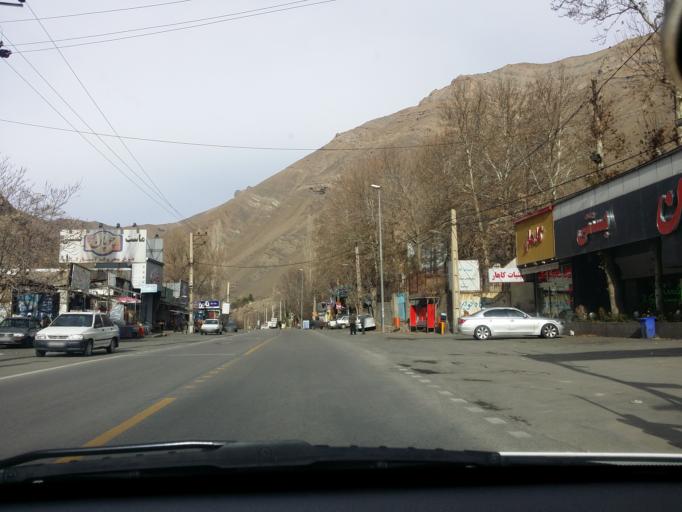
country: IR
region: Alborz
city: Karaj
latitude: 36.0357
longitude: 51.1935
